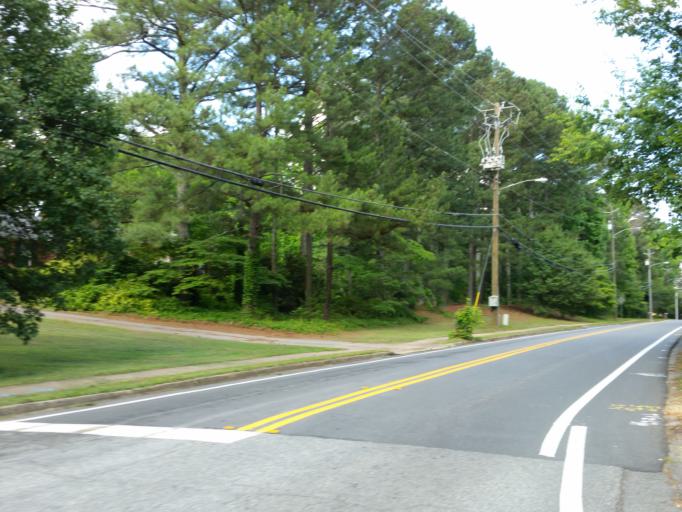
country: US
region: Georgia
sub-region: Fulton County
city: Roswell
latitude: 34.0613
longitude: -84.3609
